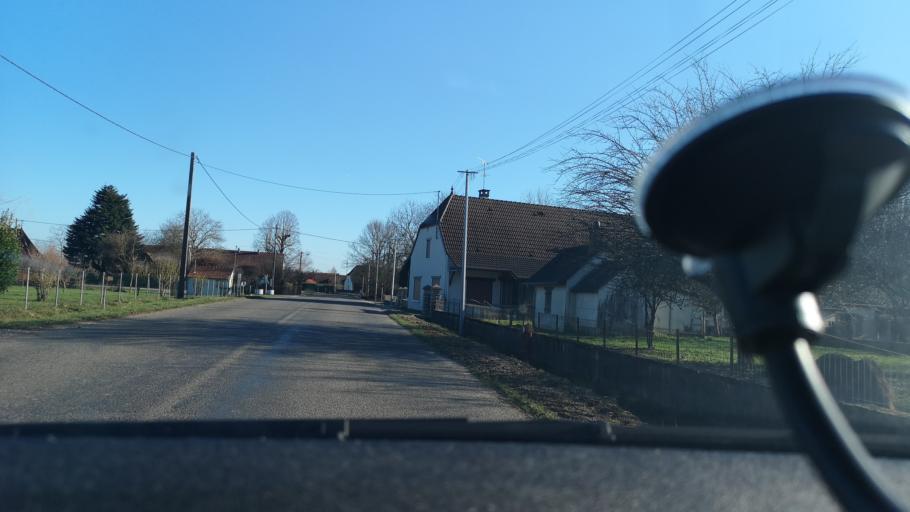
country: FR
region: Bourgogne
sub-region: Departement de Saone-et-Loire
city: Saint-Germain-du-Bois
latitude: 46.7468
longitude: 5.3270
